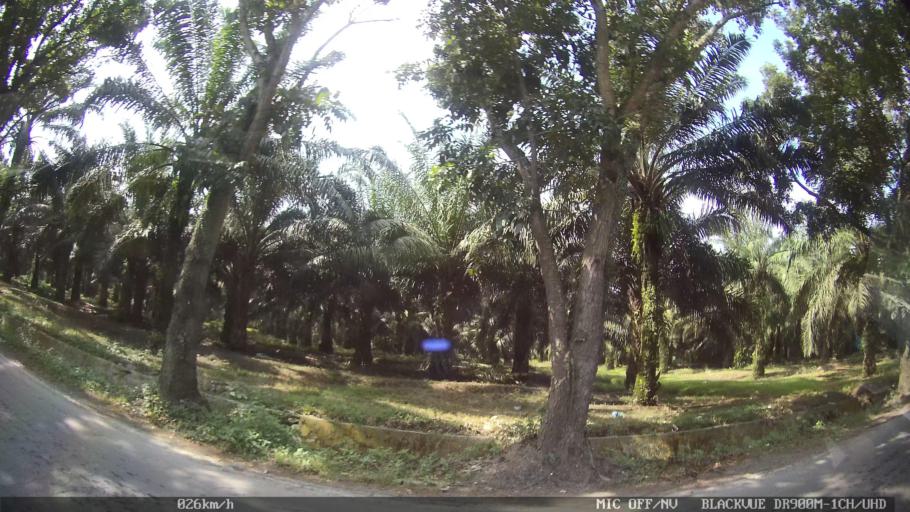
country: ID
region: North Sumatra
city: Binjai
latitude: 3.6511
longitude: 98.5256
